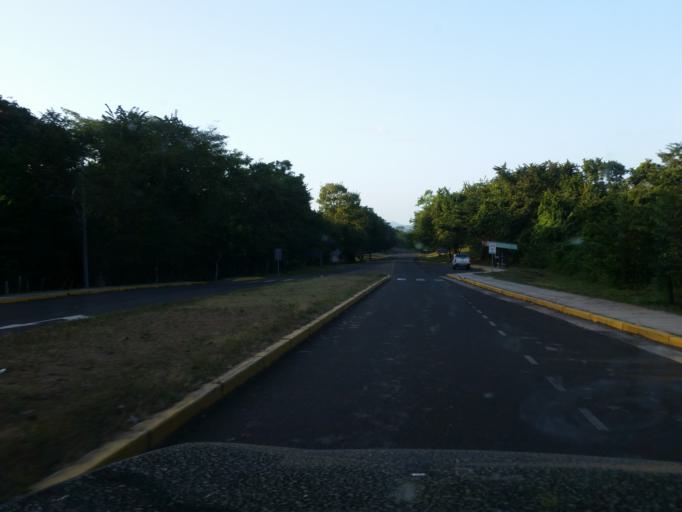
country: NI
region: Rio San Juan
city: El Almendro
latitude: 11.5858
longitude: -84.8455
